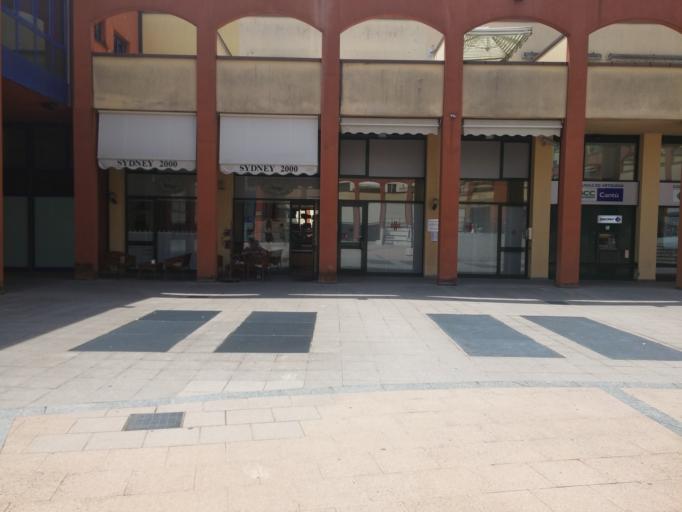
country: IT
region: Lombardy
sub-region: Provincia di Como
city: Bulgarograsso
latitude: 45.7504
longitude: 9.0086
